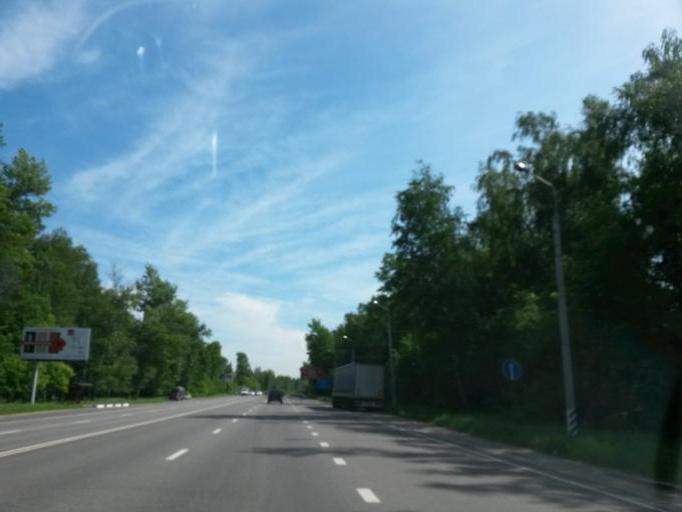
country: RU
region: Moskovskaya
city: Vostryakovo
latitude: 55.4152
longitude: 37.7803
